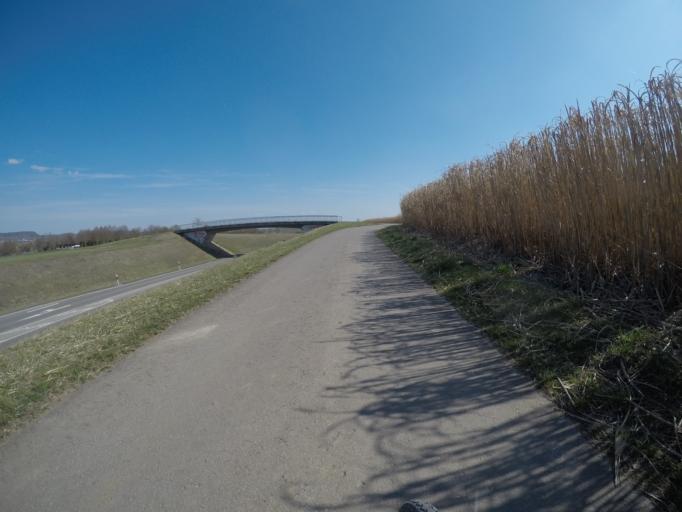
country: DE
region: Baden-Wuerttemberg
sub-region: Regierungsbezirk Stuttgart
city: Herrenberg
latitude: 48.5691
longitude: 8.8755
